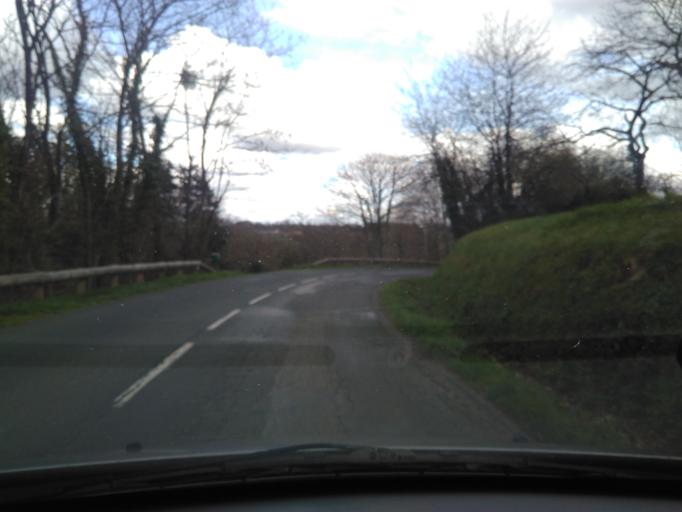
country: FR
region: Pays de la Loire
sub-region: Departement de la Vendee
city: Sainte-Cecile
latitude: 46.6889
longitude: -1.1192
